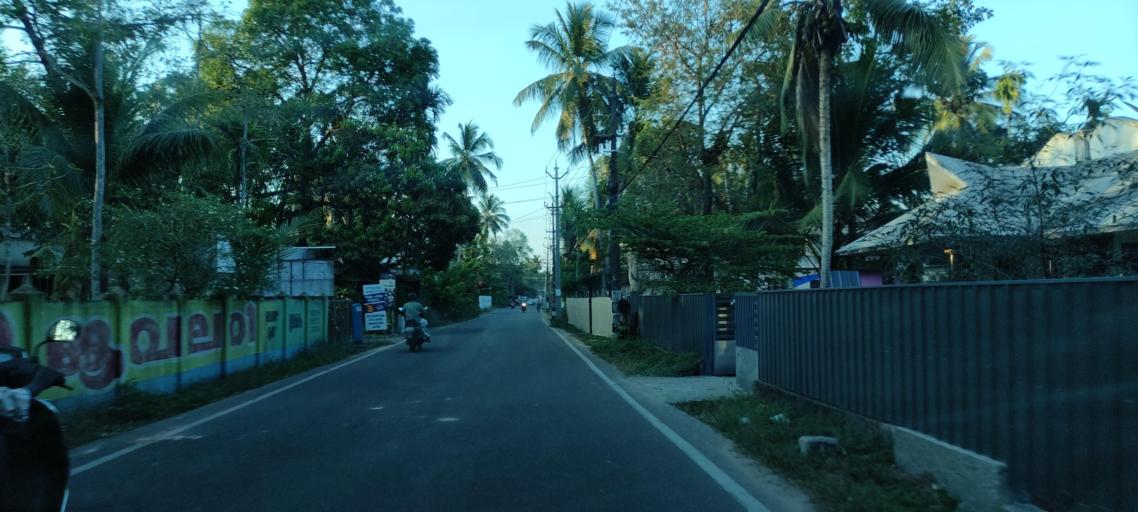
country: IN
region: Kerala
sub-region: Alappuzha
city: Kayankulam
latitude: 9.2058
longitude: 76.4625
